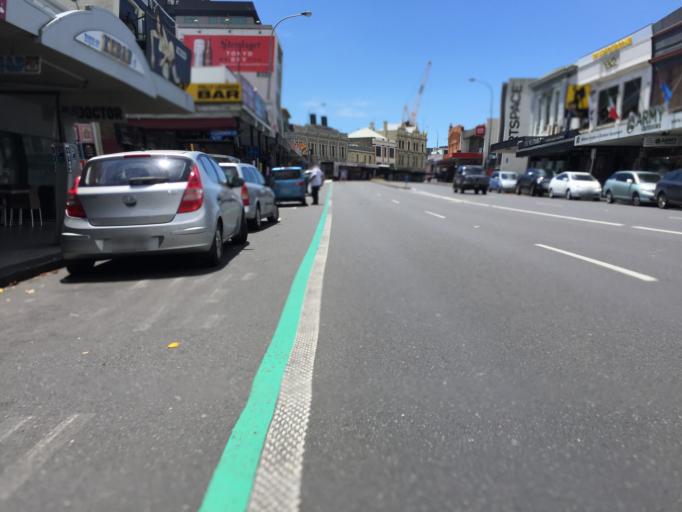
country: NZ
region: Auckland
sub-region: Auckland
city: Auckland
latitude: -36.8580
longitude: 174.7570
